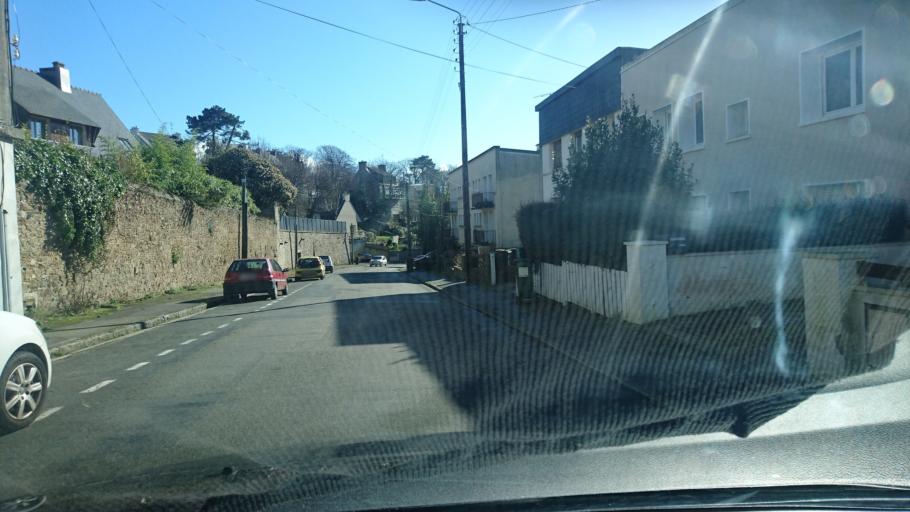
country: FR
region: Brittany
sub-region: Departement du Finistere
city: Brest
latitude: 48.3976
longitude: -4.4512
